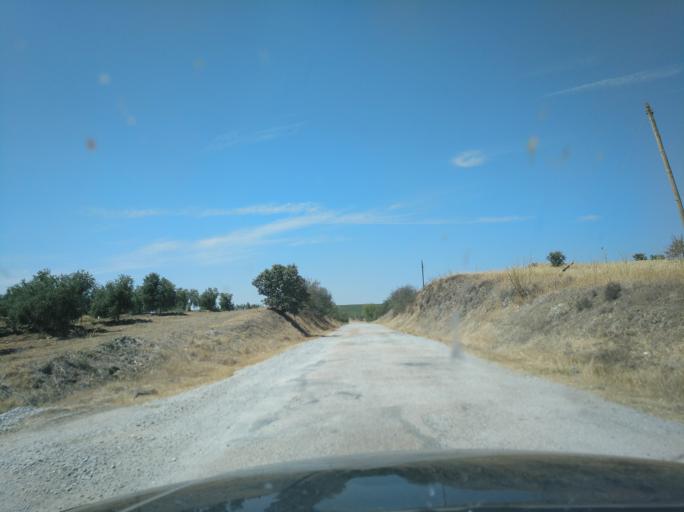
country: PT
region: Portalegre
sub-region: Campo Maior
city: Campo Maior
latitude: 38.9838
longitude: -7.0989
